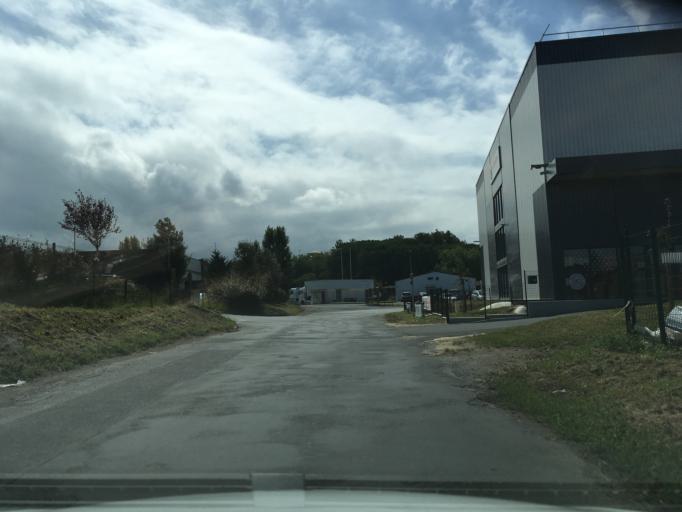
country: FR
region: Aquitaine
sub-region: Departement des Pyrenees-Atlantiques
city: Bayonne
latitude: 43.4907
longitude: -1.4573
